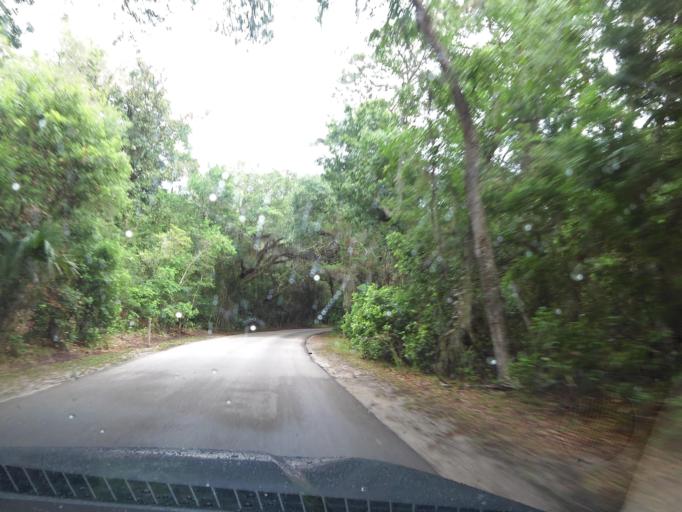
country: US
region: Florida
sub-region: Nassau County
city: Fernandina Beach
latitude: 30.6967
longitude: -81.4404
